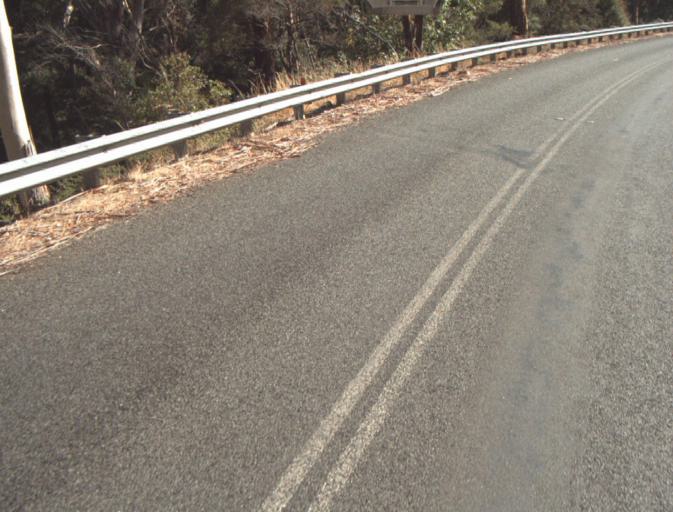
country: AU
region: Tasmania
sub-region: Dorset
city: Bridport
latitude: -41.1677
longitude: 147.2316
